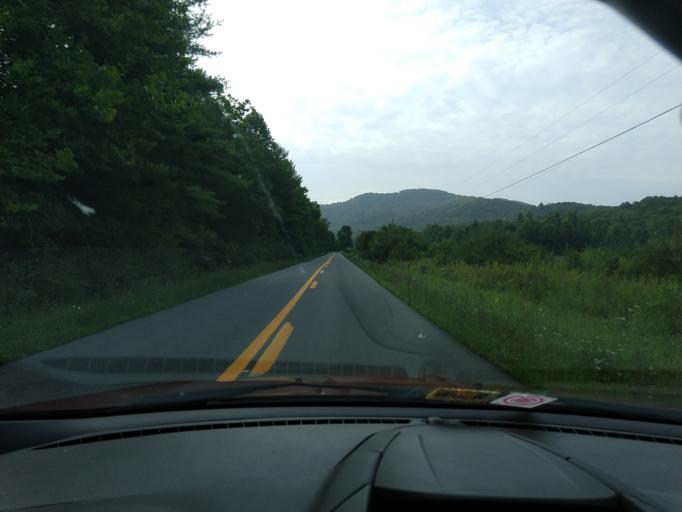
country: US
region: Virginia
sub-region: City of Covington
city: Covington
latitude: 37.9561
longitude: -80.1190
